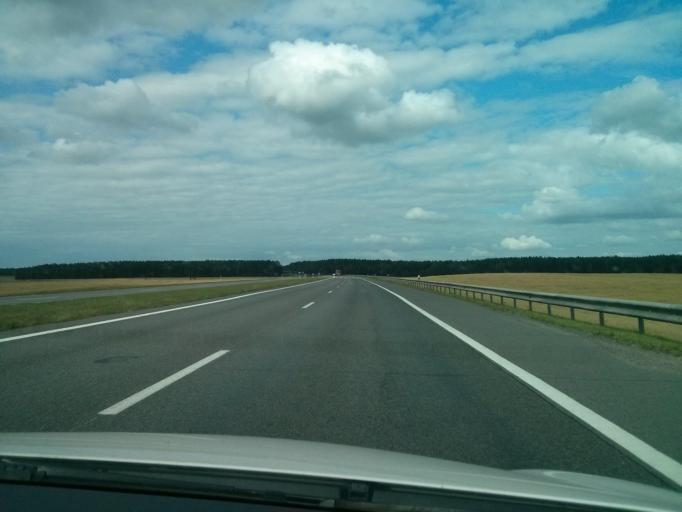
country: BY
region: Minsk
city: Zamostochcha
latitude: 53.8815
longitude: 27.9353
